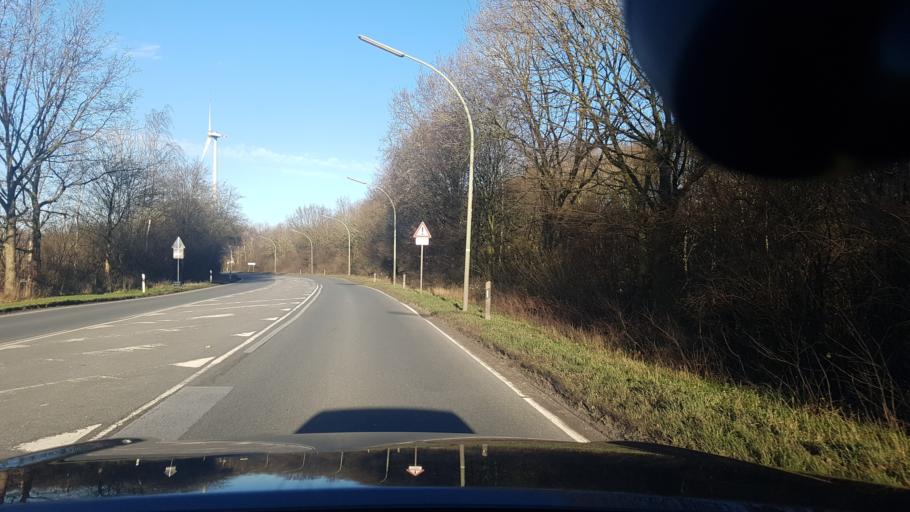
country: DE
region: Lower Saxony
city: Langen
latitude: 53.5856
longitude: 8.5695
